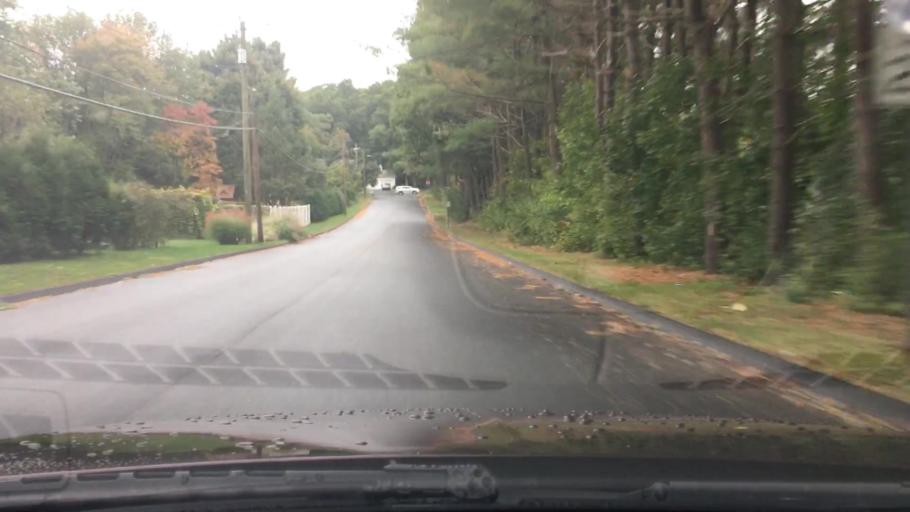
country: US
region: Connecticut
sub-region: Hartford County
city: Manchester
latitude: 41.8233
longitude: -72.5084
